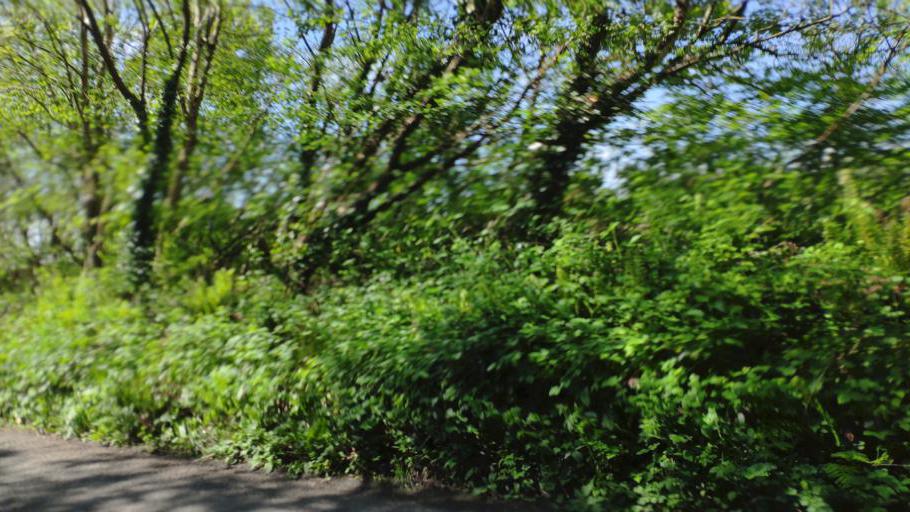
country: IE
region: Munster
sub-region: County Cork
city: Blarney
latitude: 51.9612
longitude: -8.5766
